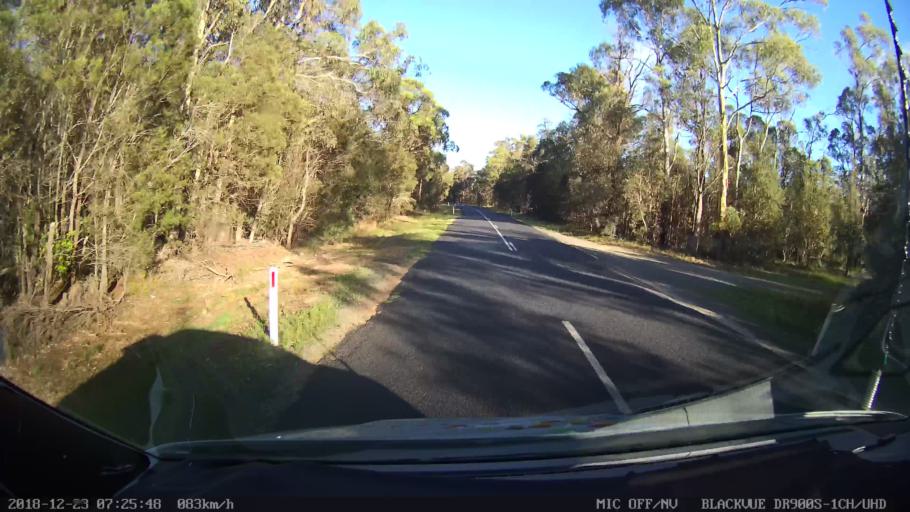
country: AU
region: New South Wales
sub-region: Armidale Dumaresq
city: Enmore
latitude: -30.4955
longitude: 152.2067
